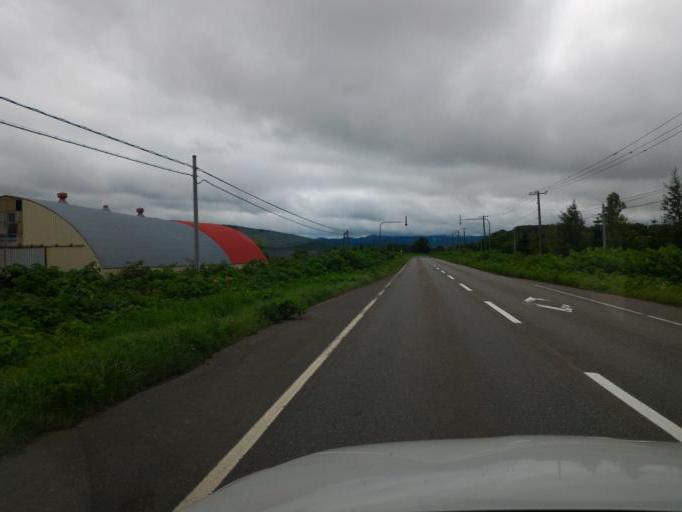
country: JP
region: Hokkaido
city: Makubetsu
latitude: 44.8791
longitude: 142.0241
